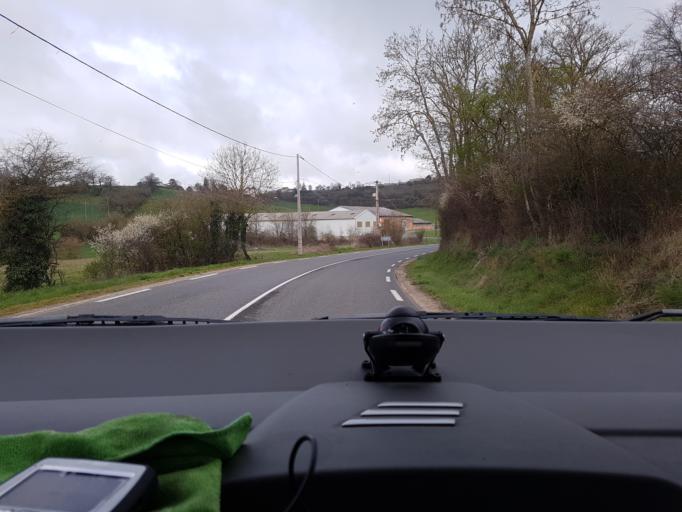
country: FR
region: Midi-Pyrenees
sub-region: Departement de l'Aveyron
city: Olemps
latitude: 44.3662
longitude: 2.5422
